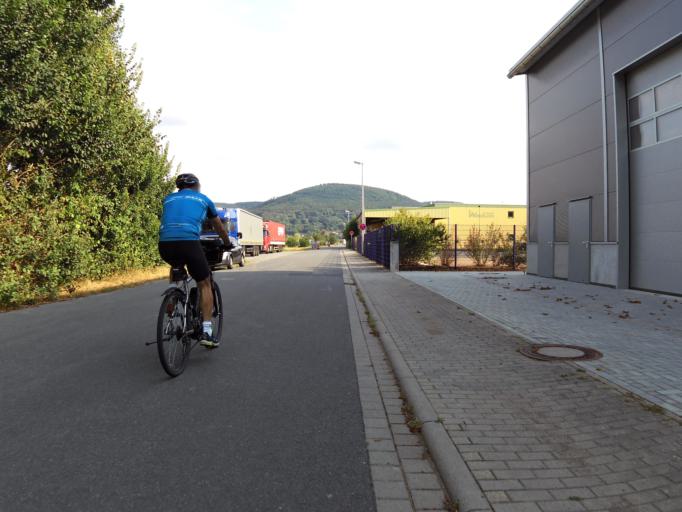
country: DE
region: Bavaria
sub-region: Regierungsbezirk Unterfranken
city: Kleinheubach
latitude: 49.7154
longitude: 9.2226
